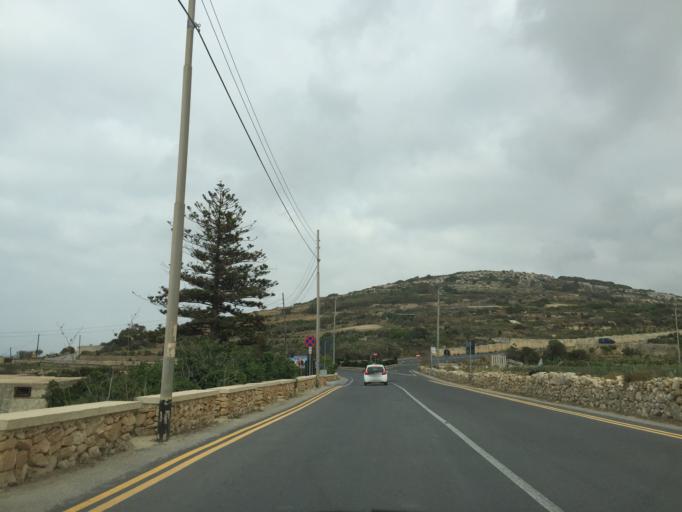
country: MT
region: L-Imgarr
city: Imgarr
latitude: 35.9307
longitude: 14.3486
